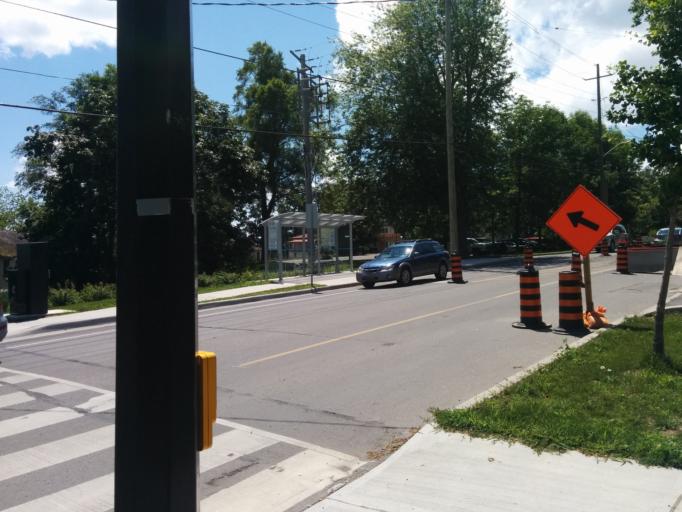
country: CA
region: Ontario
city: Kingston
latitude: 44.2216
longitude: -76.5065
